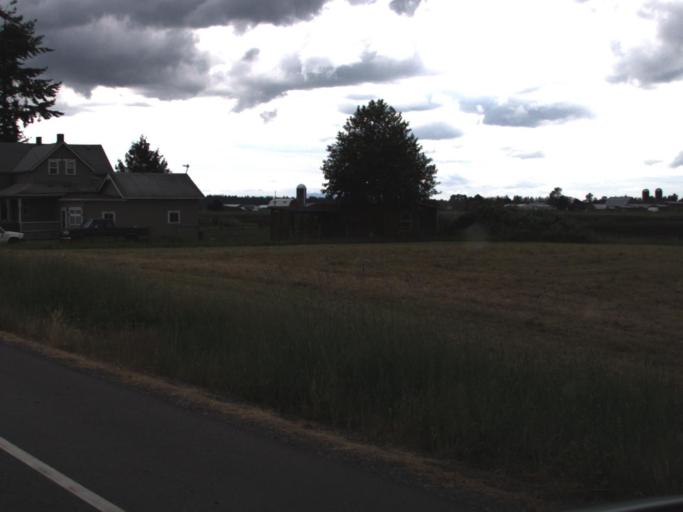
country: CA
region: British Columbia
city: Aldergrove
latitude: 48.9991
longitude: -122.4851
